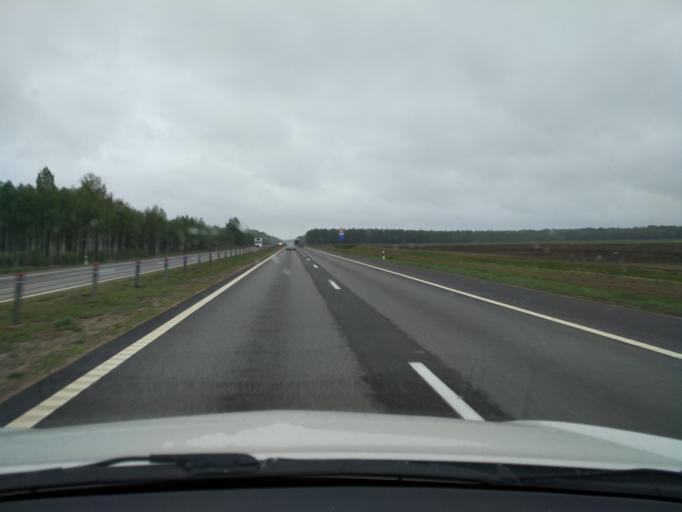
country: BY
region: Mogilev
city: Yalizava
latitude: 53.2683
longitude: 28.8781
